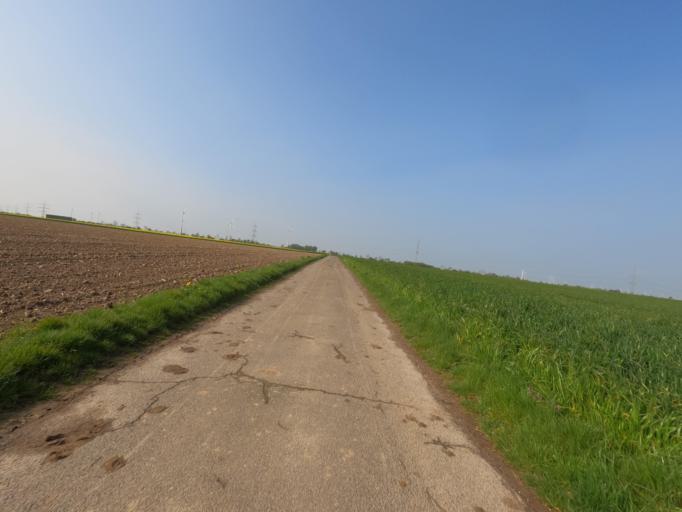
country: DE
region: North Rhine-Westphalia
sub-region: Regierungsbezirk Koln
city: Heinsberg
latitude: 51.0371
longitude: 6.1226
